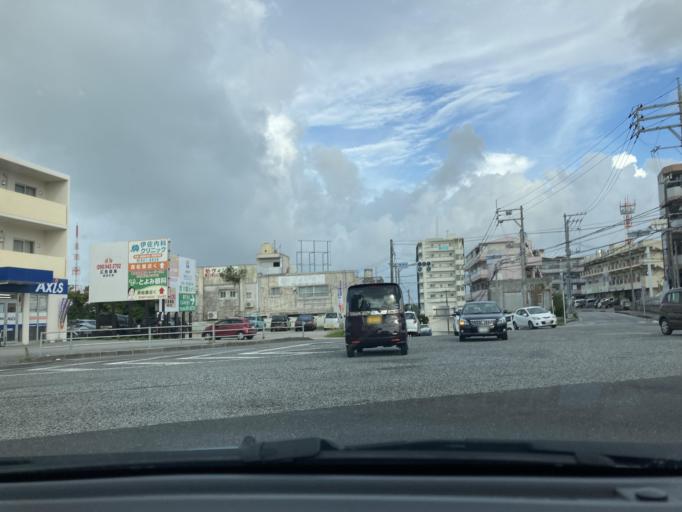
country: JP
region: Okinawa
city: Tomigusuku
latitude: 26.1769
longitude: 127.6820
